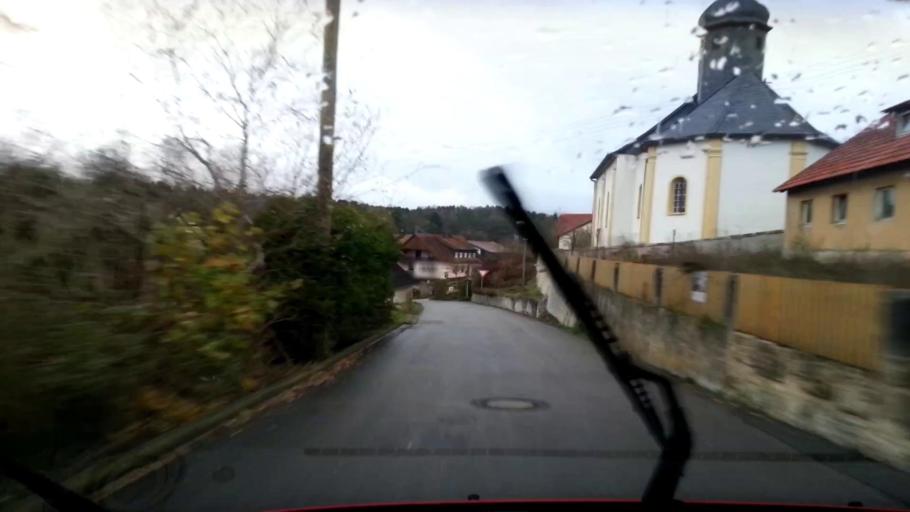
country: DE
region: Bavaria
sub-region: Upper Franconia
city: Aufsess
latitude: 49.9272
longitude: 11.2200
